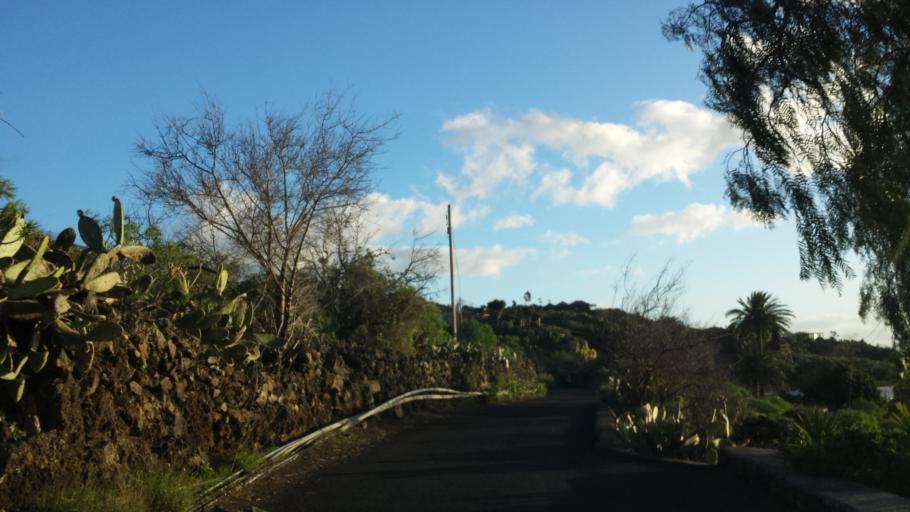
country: ES
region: Canary Islands
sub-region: Provincia de Santa Cruz de Tenerife
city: El Paso
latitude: 28.6138
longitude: -17.8910
